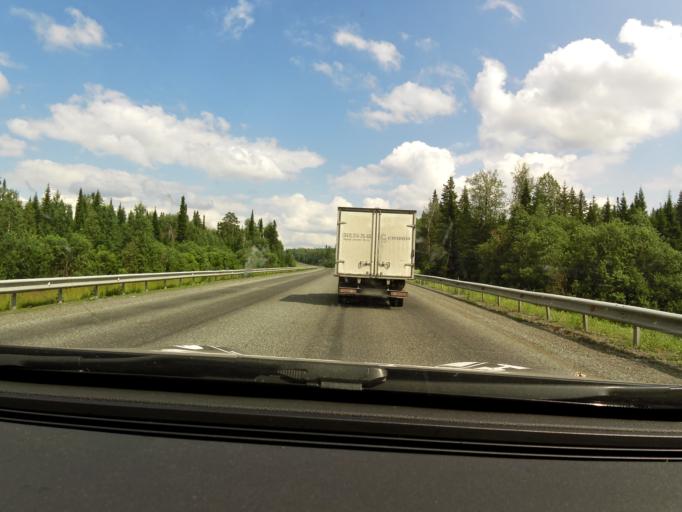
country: RU
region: Sverdlovsk
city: Arti
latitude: 56.7860
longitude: 58.5222
